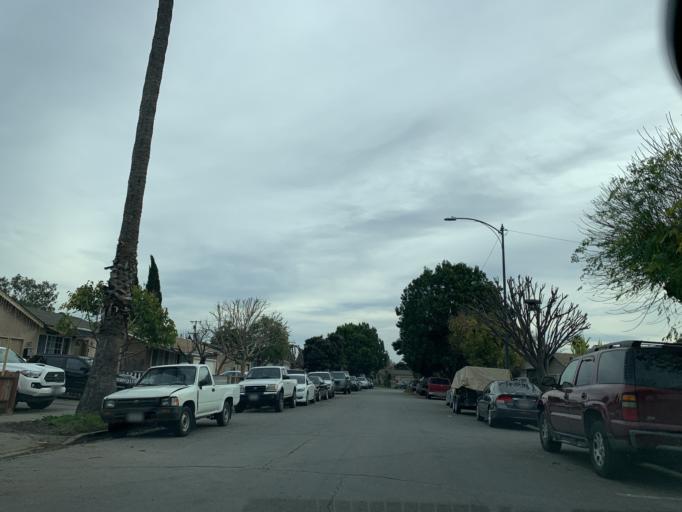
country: US
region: California
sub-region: Santa Clara County
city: Alum Rock
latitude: 37.3497
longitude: -121.8432
